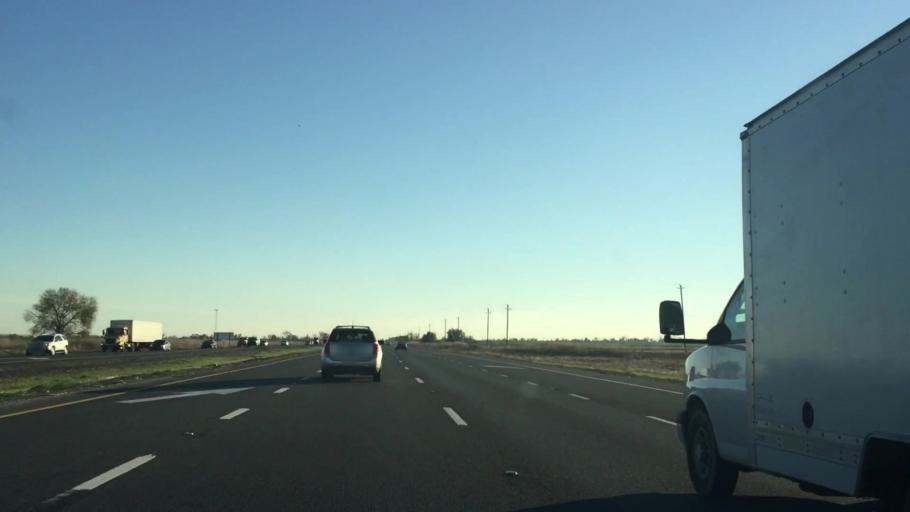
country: US
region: California
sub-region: Sacramento County
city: Elverta
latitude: 38.8367
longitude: -121.5439
